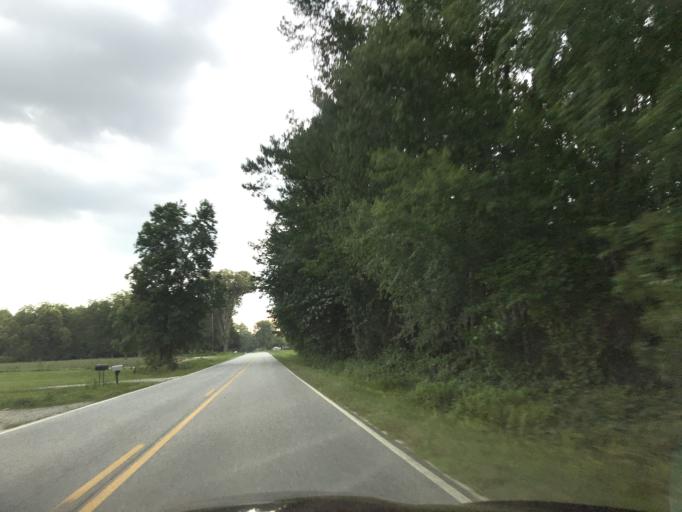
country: US
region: North Carolina
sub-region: Johnston County
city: Wilsons Mills
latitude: 35.5425
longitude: -78.4165
